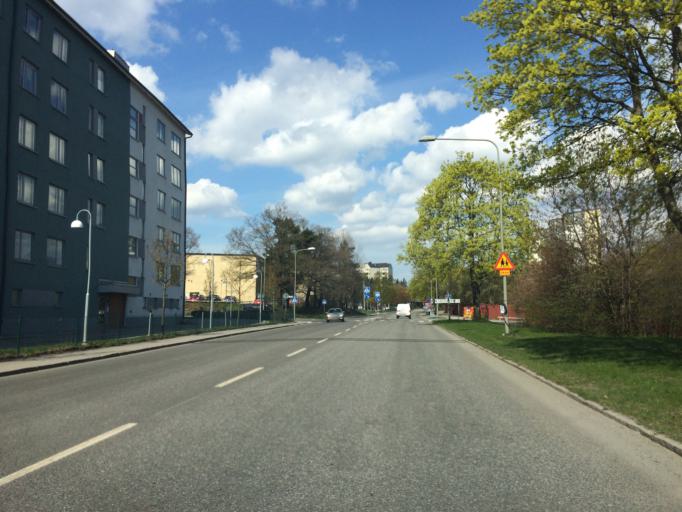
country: SE
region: Stockholm
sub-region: Huddinge Kommun
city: Segeltorp
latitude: 59.2918
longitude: 17.9796
